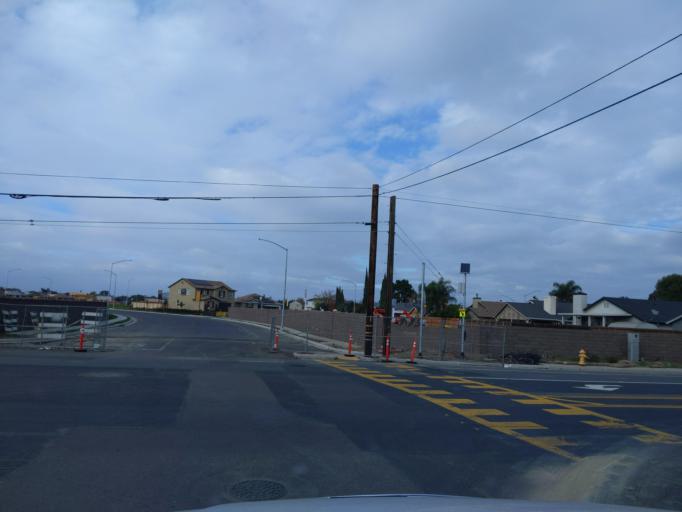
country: US
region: California
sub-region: San Joaquin County
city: August
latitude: 37.9860
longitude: -121.2754
